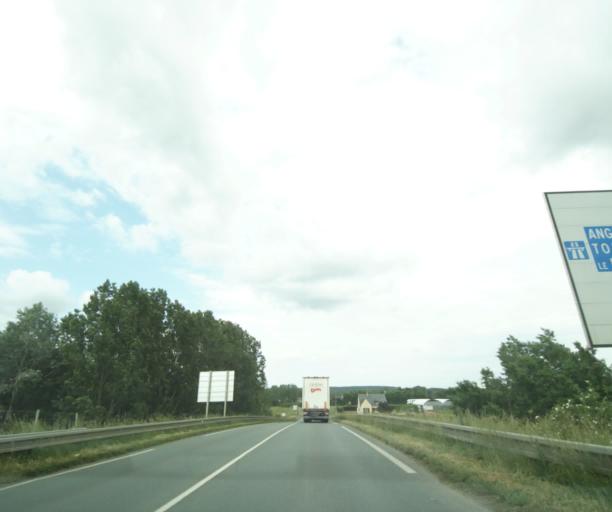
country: FR
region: Pays de la Loire
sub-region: Departement de Maine-et-Loire
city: Vivy
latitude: 47.3066
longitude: -0.0337
